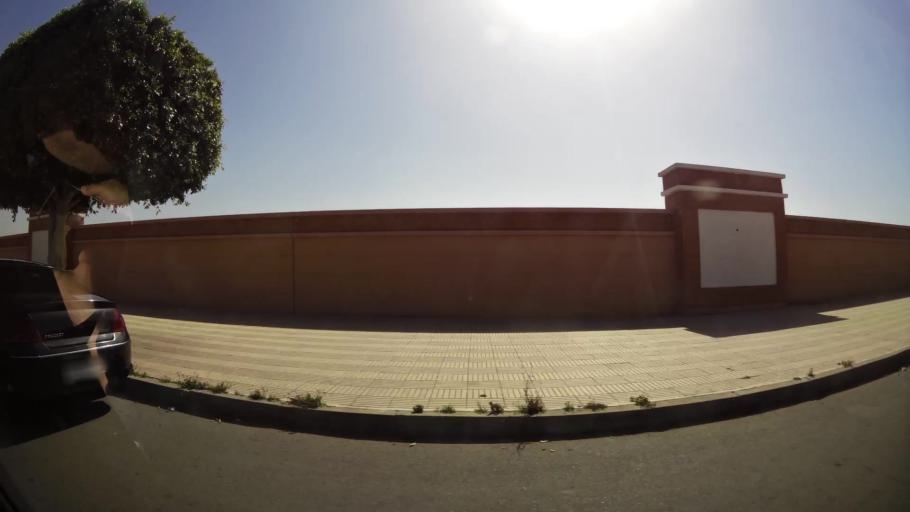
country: MA
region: Souss-Massa-Draa
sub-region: Inezgane-Ait Mellou
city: Inezgane
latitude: 30.3640
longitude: -9.5443
